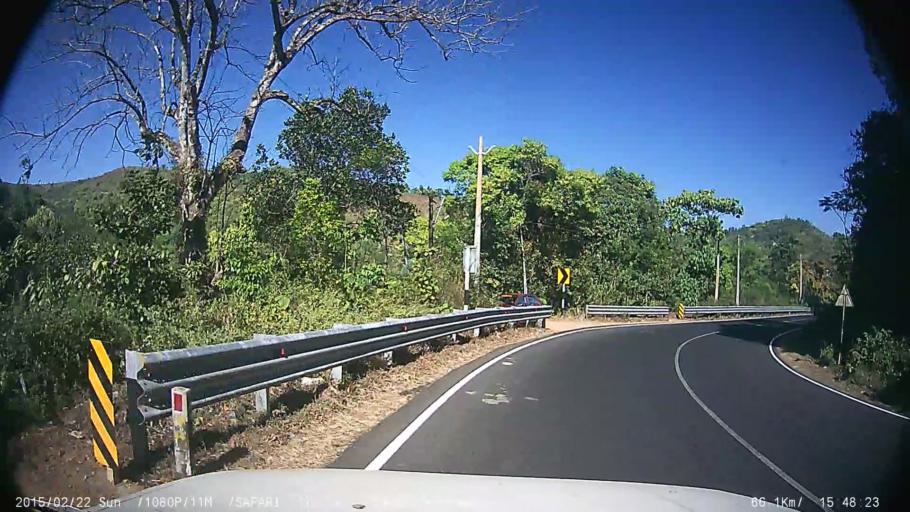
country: IN
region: Kerala
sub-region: Kottayam
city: Erattupetta
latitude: 9.5733
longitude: 76.9925
